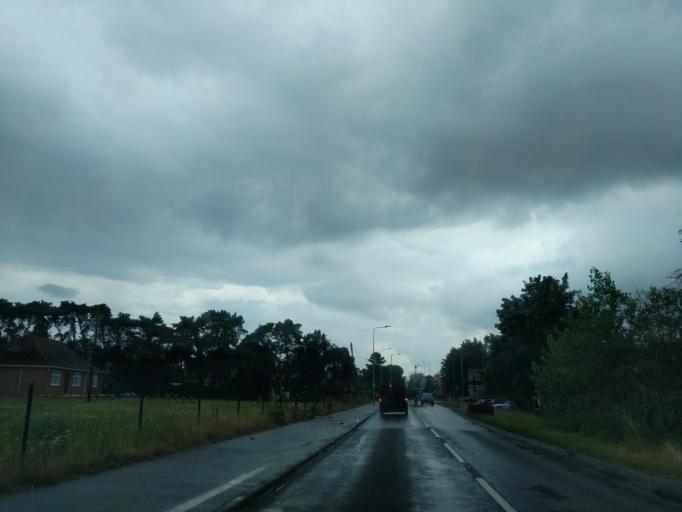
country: GB
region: England
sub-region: Suffolk
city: Lakenheath
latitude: 52.3563
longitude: 0.5146
